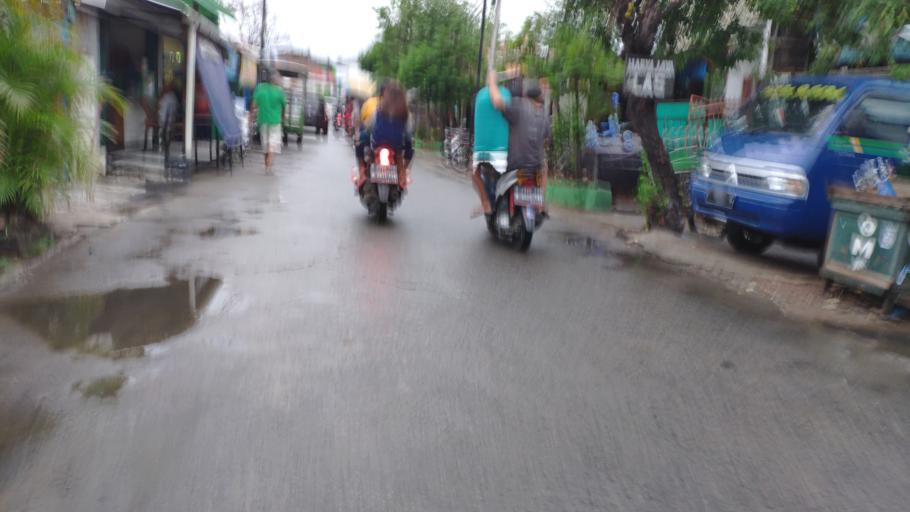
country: ID
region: Jakarta Raya
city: Jakarta
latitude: -6.2078
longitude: 106.8659
